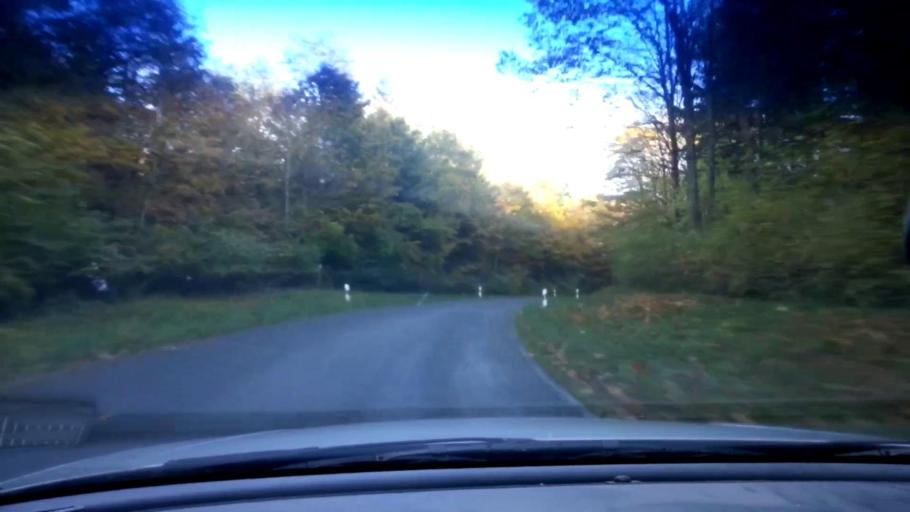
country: DE
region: Bavaria
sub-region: Upper Franconia
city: Heiligenstadt
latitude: 49.8753
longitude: 11.1828
